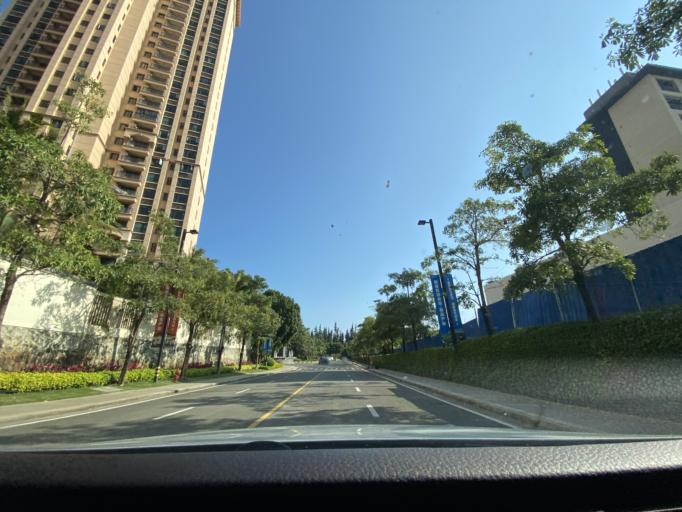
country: CN
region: Hainan
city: Yingzhou
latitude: 18.4113
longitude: 109.8864
